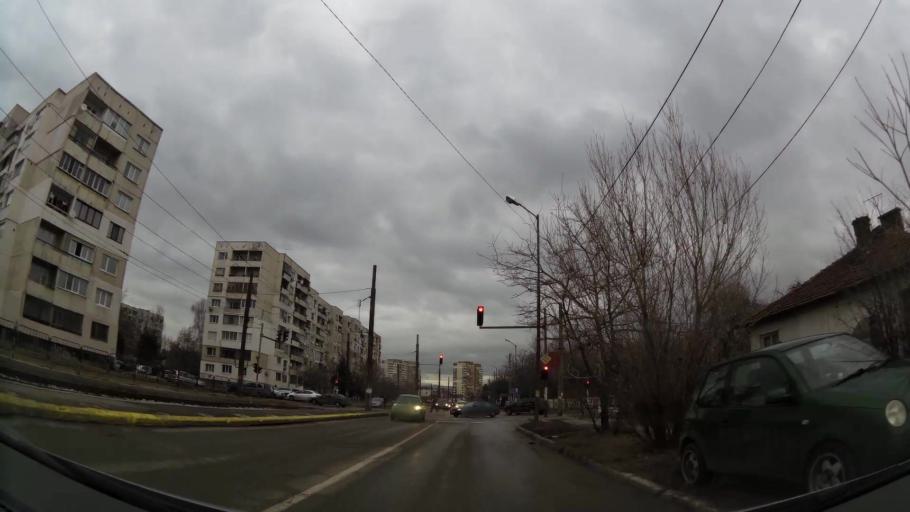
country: BG
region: Sofia-Capital
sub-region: Stolichna Obshtina
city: Sofia
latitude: 42.7298
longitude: 23.2932
